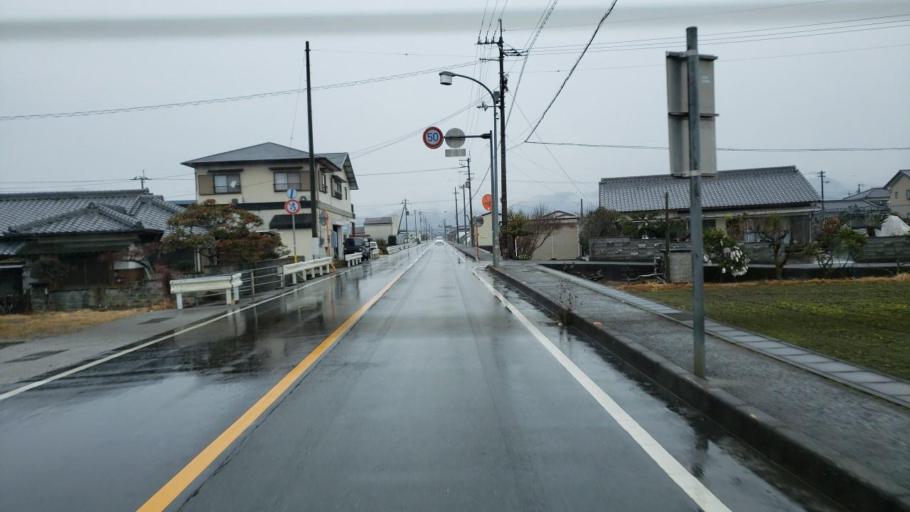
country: JP
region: Tokushima
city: Kamojimacho-jogejima
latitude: 34.0764
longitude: 134.2812
